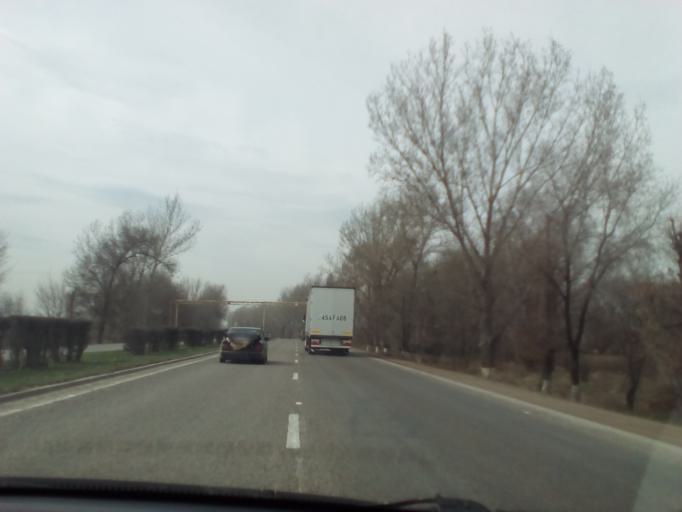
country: KZ
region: Almaty Oblysy
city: Burunday
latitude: 43.2233
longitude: 76.6107
